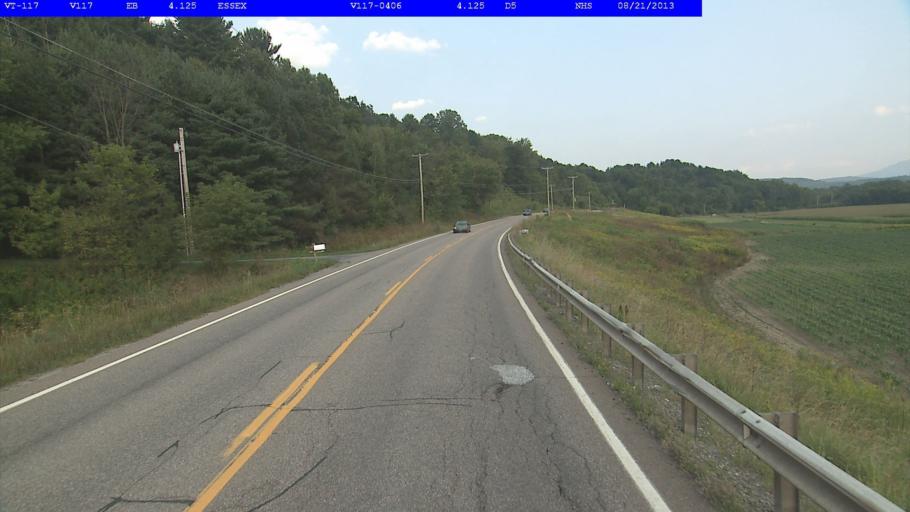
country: US
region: Vermont
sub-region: Chittenden County
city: Jericho
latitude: 44.4737
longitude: -73.0351
